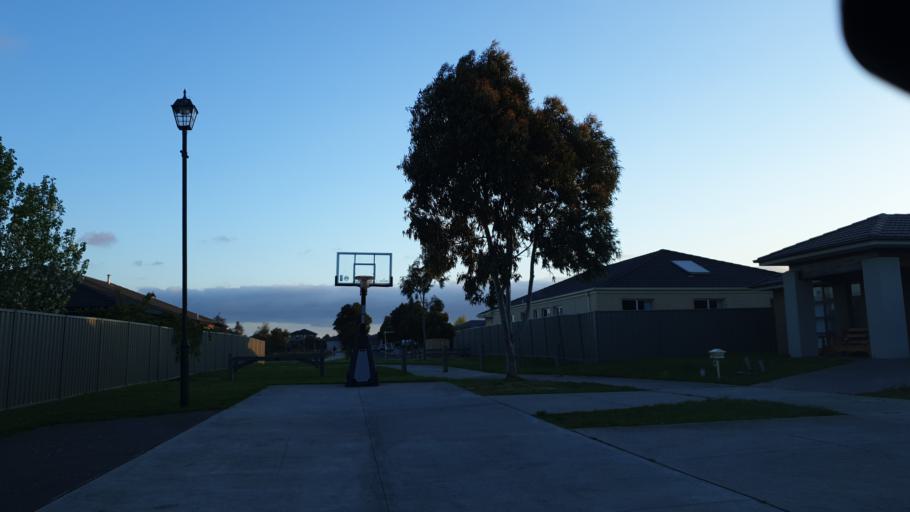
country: AU
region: Victoria
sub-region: Casey
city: Cranbourne East
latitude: -38.1091
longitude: 145.3083
